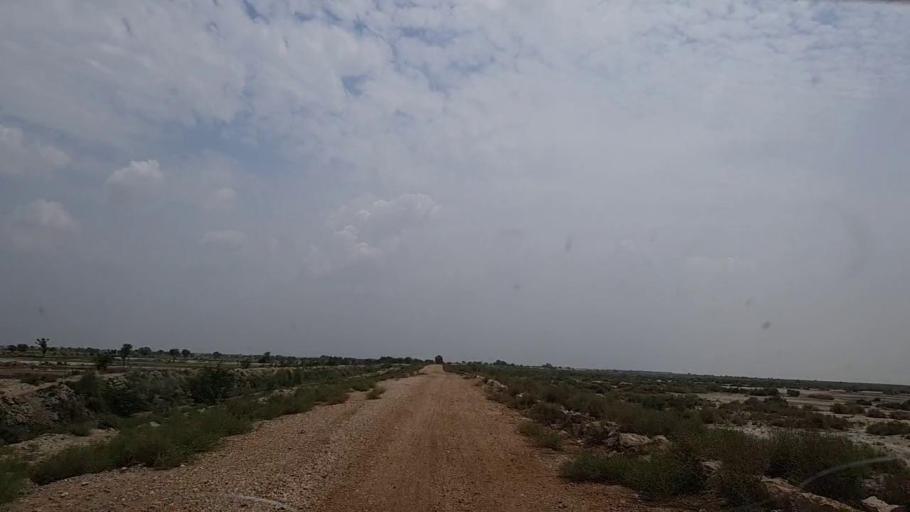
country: PK
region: Sindh
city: Phulji
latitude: 26.8363
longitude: 67.6177
